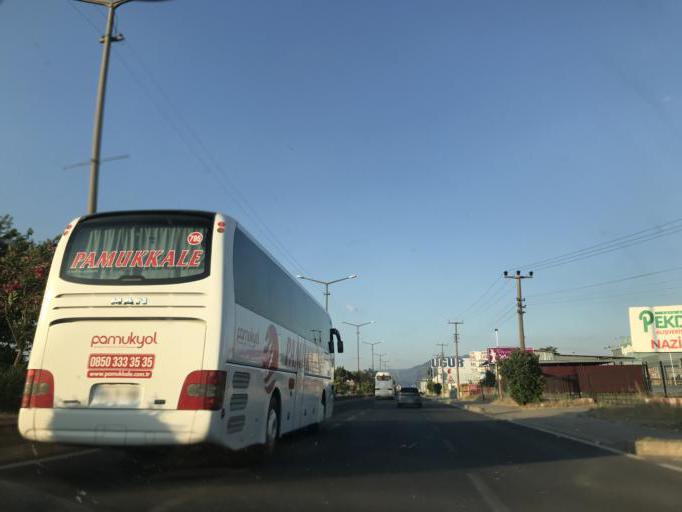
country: TR
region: Aydin
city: Nazilli
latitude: 37.9037
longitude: 28.2990
